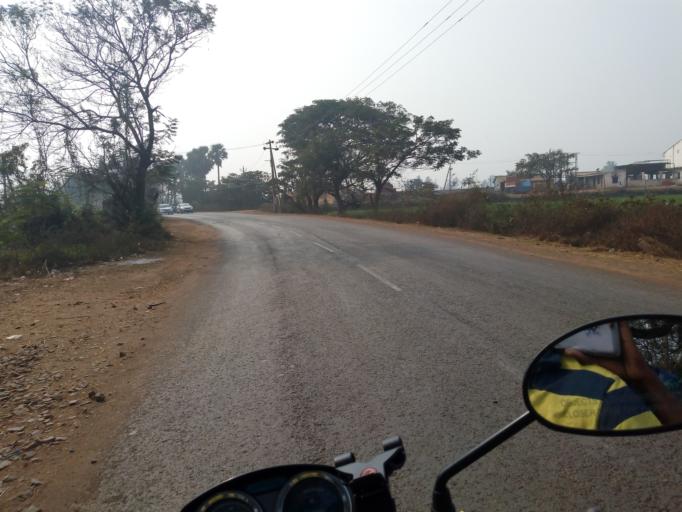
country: IN
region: Andhra Pradesh
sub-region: West Godavari
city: Tadepallegudem
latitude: 16.8091
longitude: 81.4085
